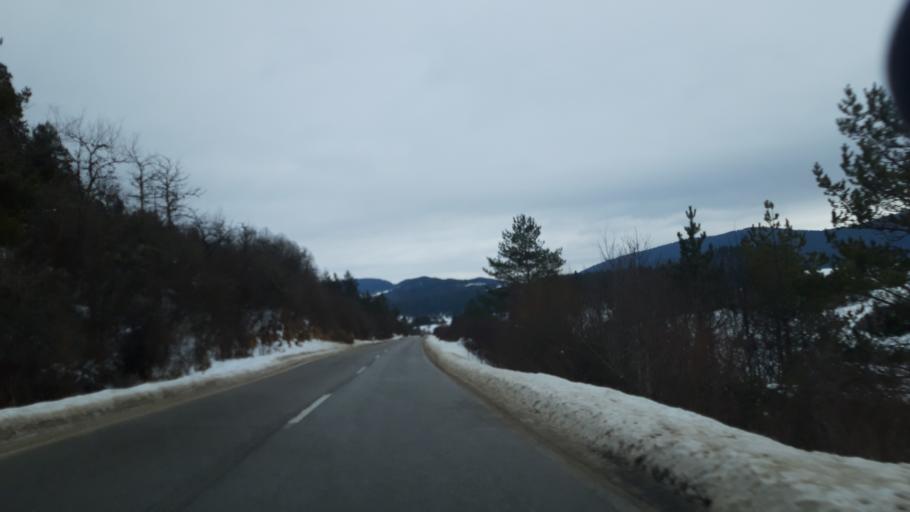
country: BA
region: Republika Srpska
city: Han Pijesak
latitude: 44.0143
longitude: 18.8855
